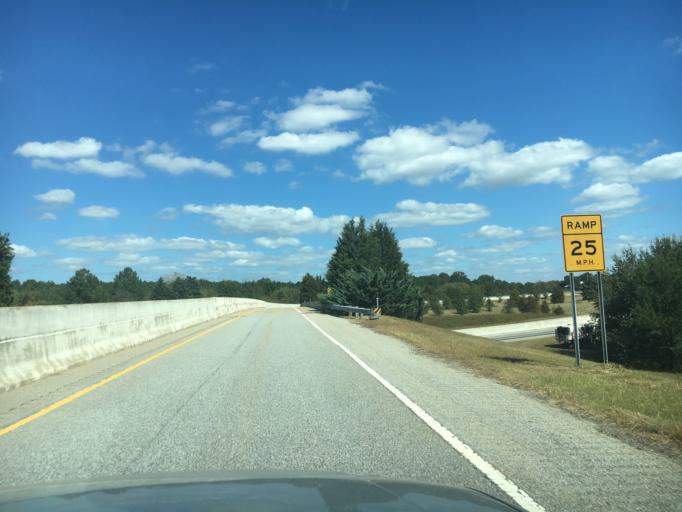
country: US
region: South Carolina
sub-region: Spartanburg County
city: Valley Falls
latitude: 35.0102
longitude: -81.9150
